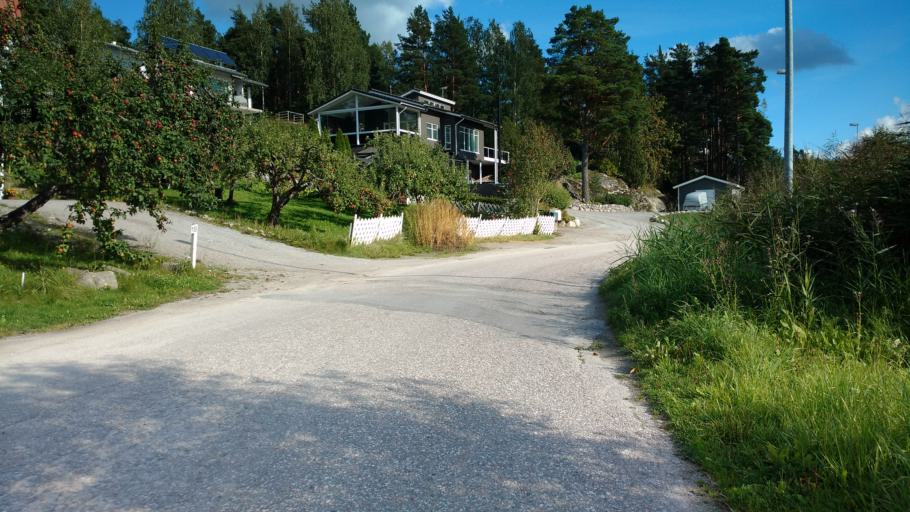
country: FI
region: Varsinais-Suomi
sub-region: Salo
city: Salo
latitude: 60.3793
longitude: 23.1674
